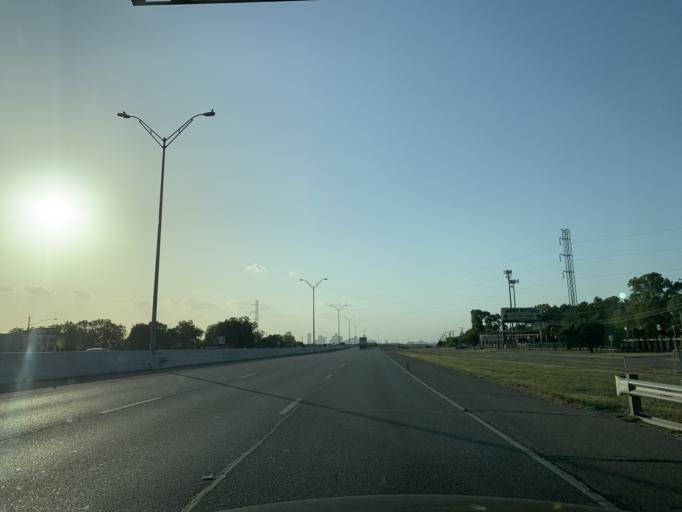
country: US
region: Texas
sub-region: Dallas County
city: Hutchins
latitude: 32.7296
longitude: -96.7076
